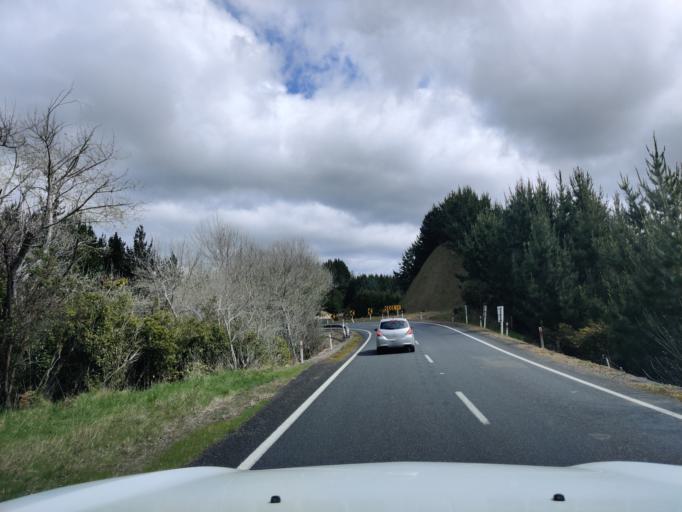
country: NZ
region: Manawatu-Wanganui
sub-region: Wanganui District
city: Wanganui
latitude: -39.7930
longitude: 175.2102
